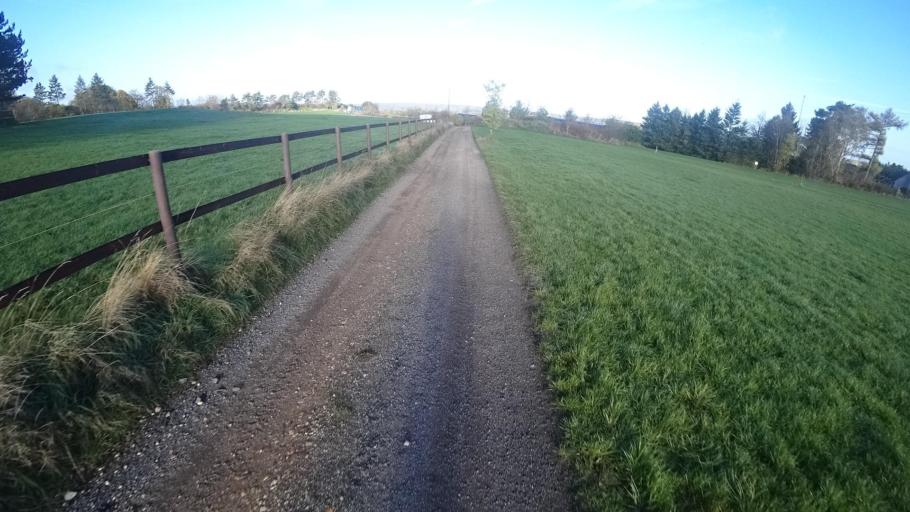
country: DE
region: Rheinland-Pfalz
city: Lind
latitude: 50.5281
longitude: 6.9283
